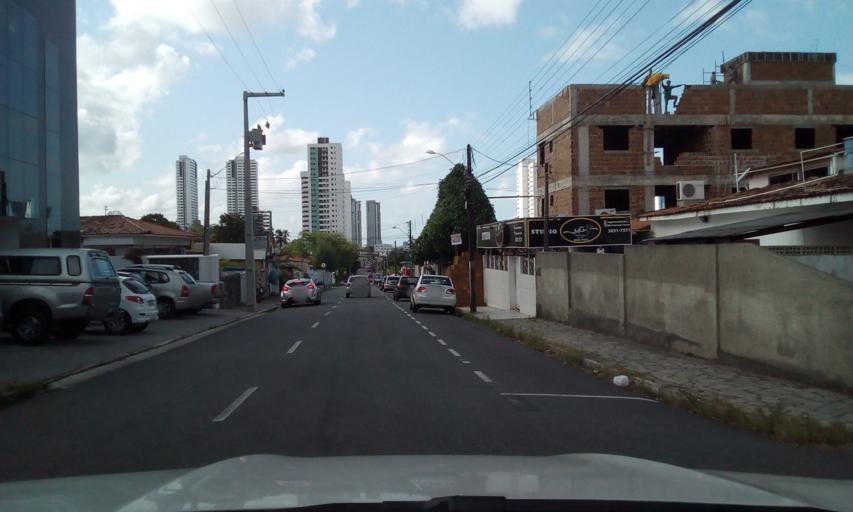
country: BR
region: Paraiba
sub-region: Joao Pessoa
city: Joao Pessoa
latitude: -7.1175
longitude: -34.8476
